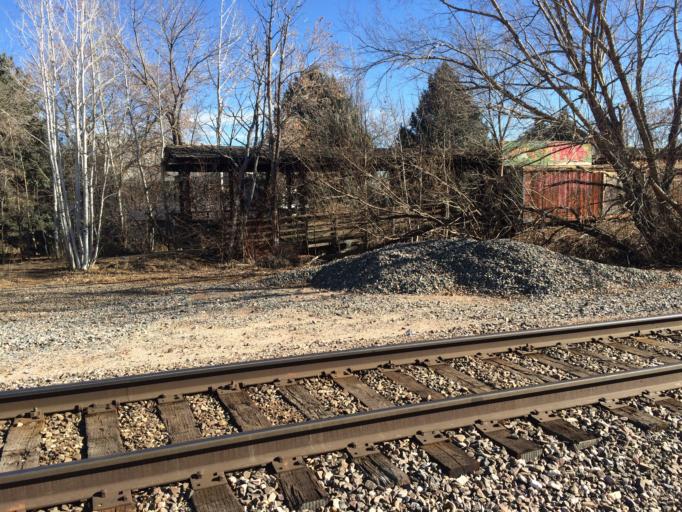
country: US
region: Colorado
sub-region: Boulder County
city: Louisville
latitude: 39.9865
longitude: -105.1319
